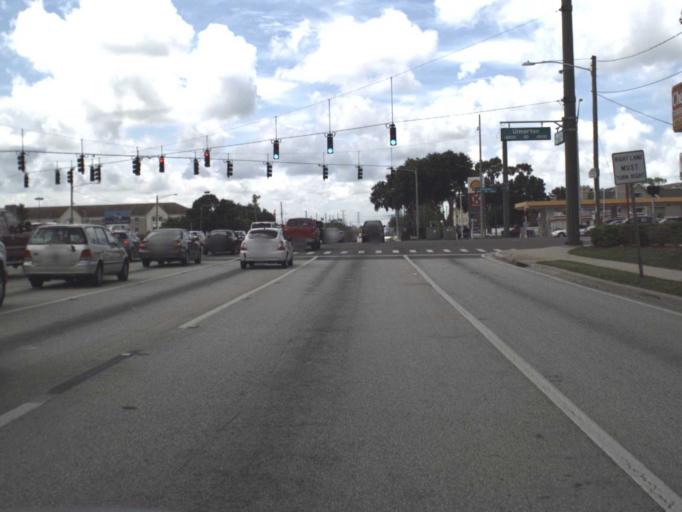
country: US
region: Florida
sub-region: Pinellas County
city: South Highpoint
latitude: 27.8946
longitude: -82.7005
